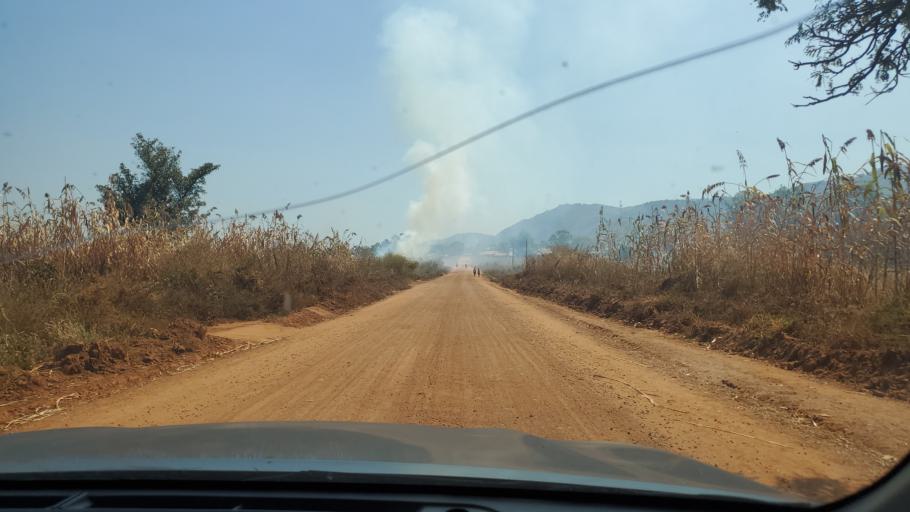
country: NG
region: Niger
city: Gawu Babangida
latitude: 9.2184
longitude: 6.8418
